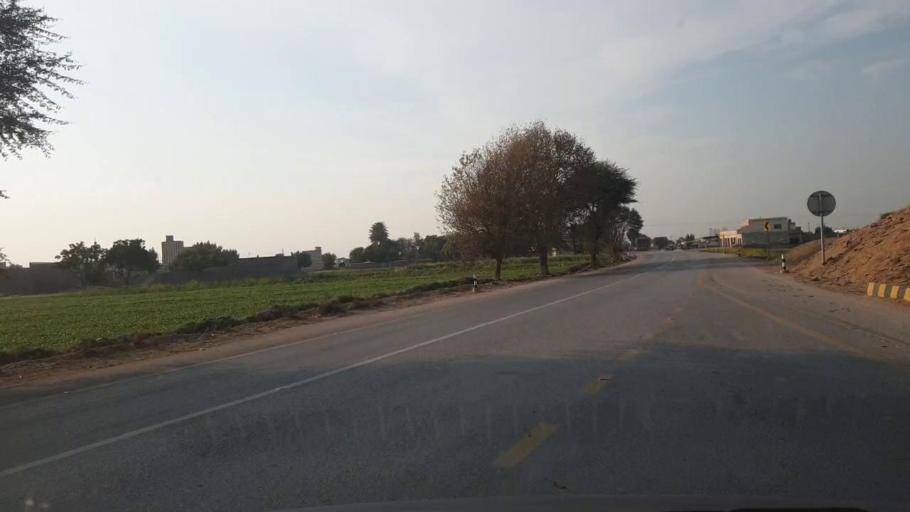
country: PK
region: Sindh
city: Shahpur Chakar
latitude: 26.1639
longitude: 68.6291
